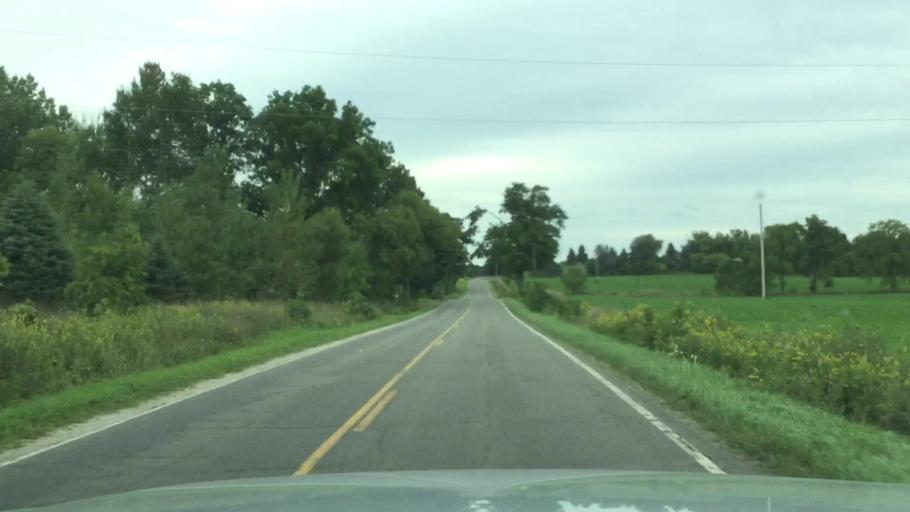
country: US
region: Michigan
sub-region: Shiawassee County
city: Durand
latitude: 42.8605
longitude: -84.0422
